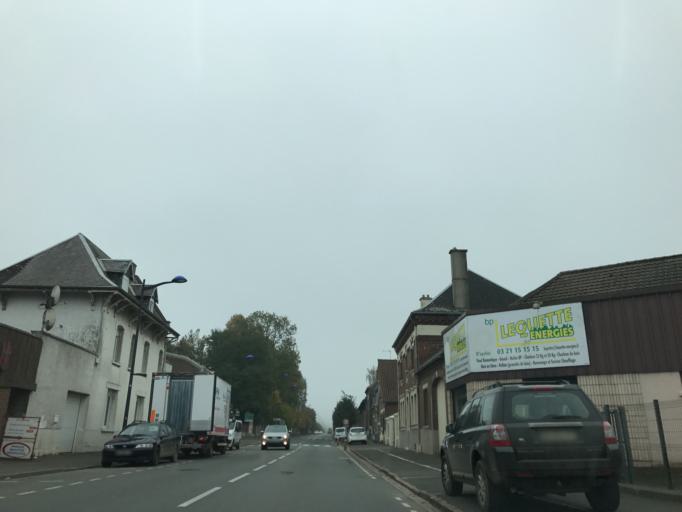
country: FR
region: Nord-Pas-de-Calais
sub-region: Departement du Pas-de-Calais
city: Bapaume
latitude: 50.0984
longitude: 2.8564
